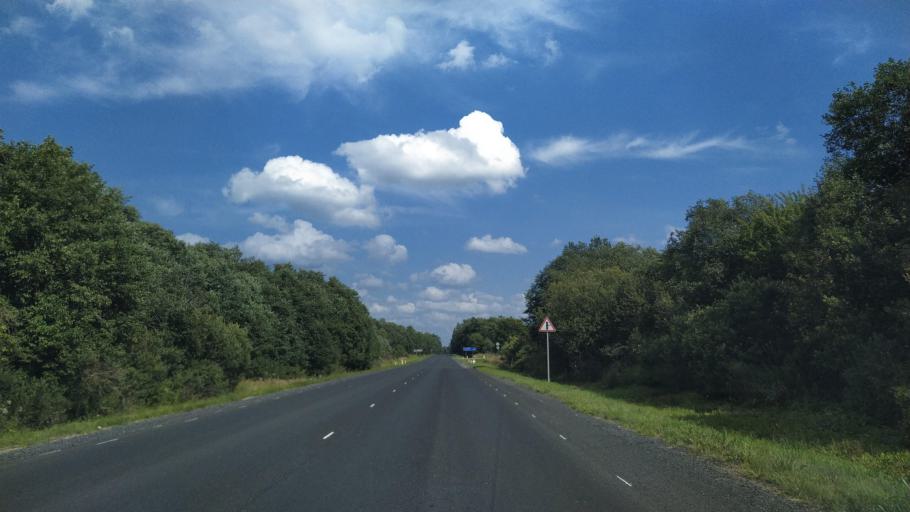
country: RU
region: Pskov
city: Porkhov
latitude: 57.7279
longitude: 29.3147
